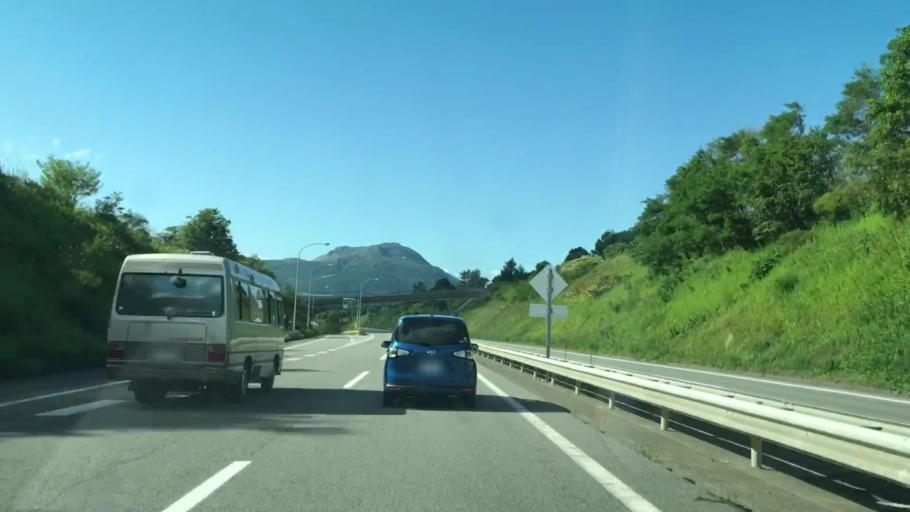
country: JP
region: Hokkaido
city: Date
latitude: 42.4792
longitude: 140.8997
